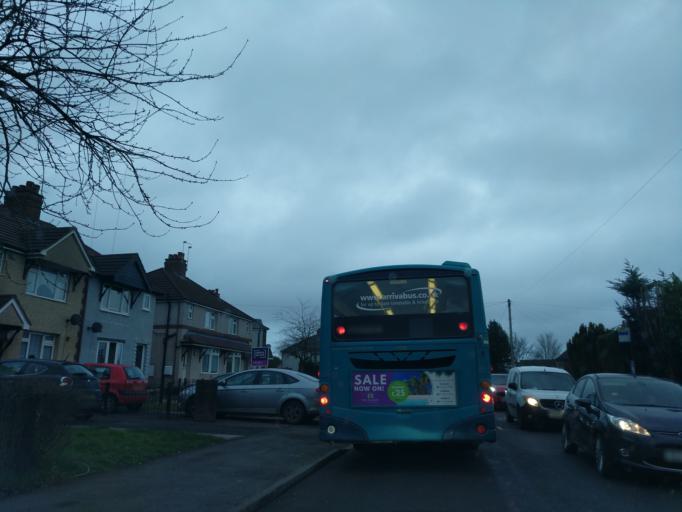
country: GB
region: England
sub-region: Staffordshire
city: Cannock
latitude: 52.7242
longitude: -2.0154
